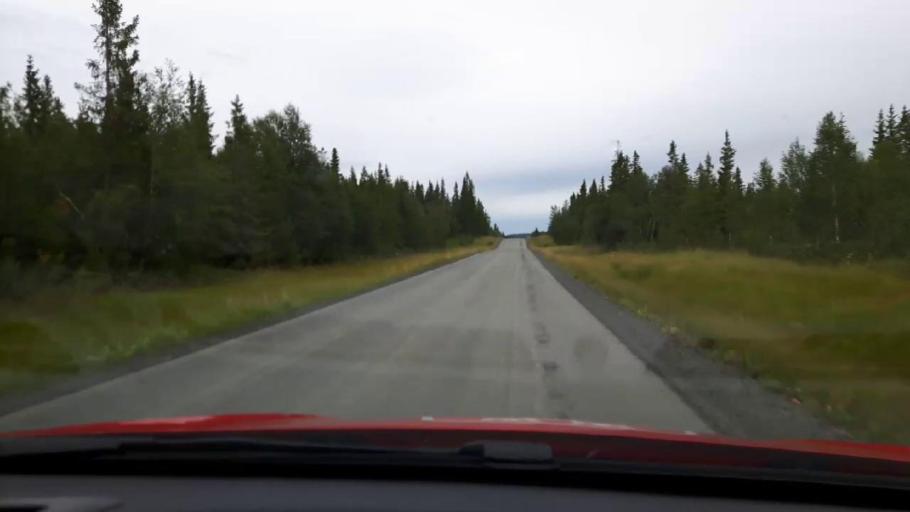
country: SE
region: Jaemtland
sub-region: Are Kommun
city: Are
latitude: 63.4432
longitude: 13.2416
